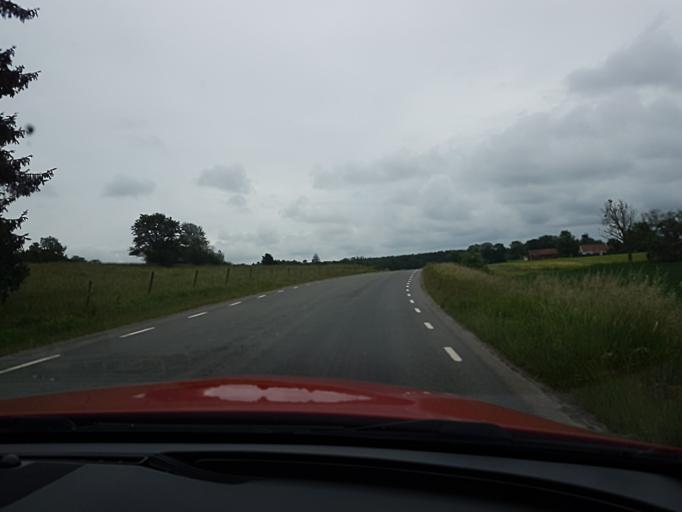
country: SE
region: Vaestra Goetaland
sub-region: Skovde Kommun
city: Skoevde
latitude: 58.3651
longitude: 13.9461
